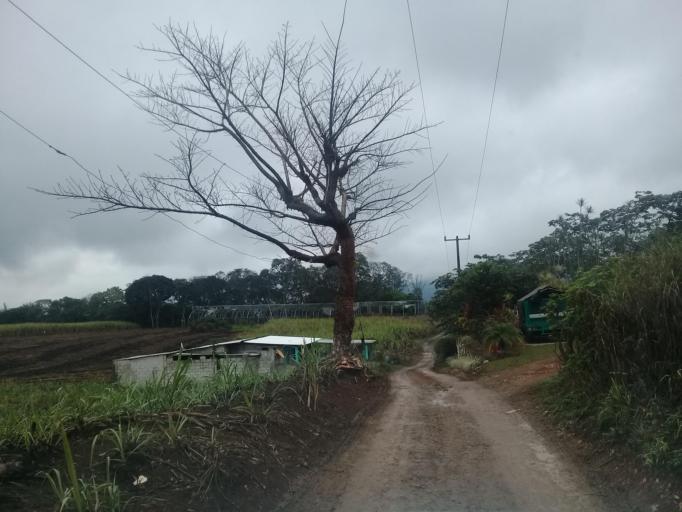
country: MX
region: Veracruz
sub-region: Amatlan de los Reyes
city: Trapiche Viejo
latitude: 18.8248
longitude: -96.9567
